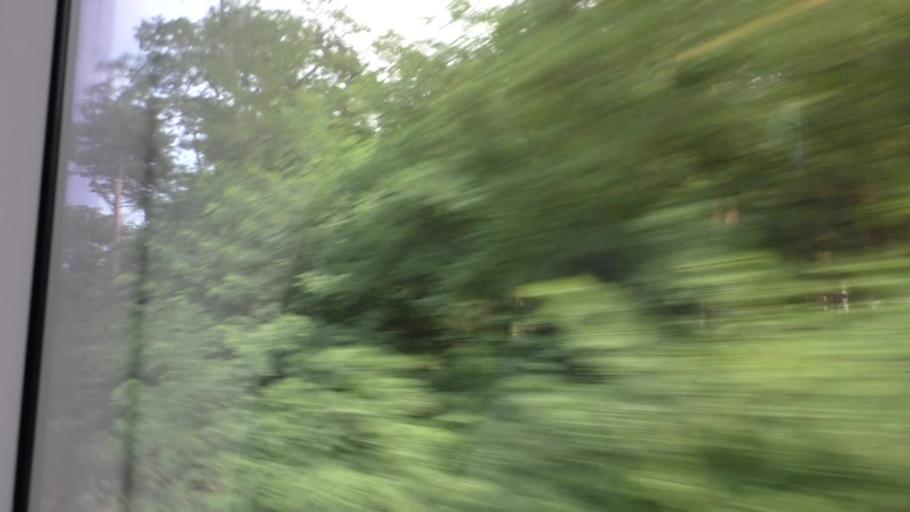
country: DE
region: Brandenburg
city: Mixdorf
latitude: 52.1839
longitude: 14.3857
